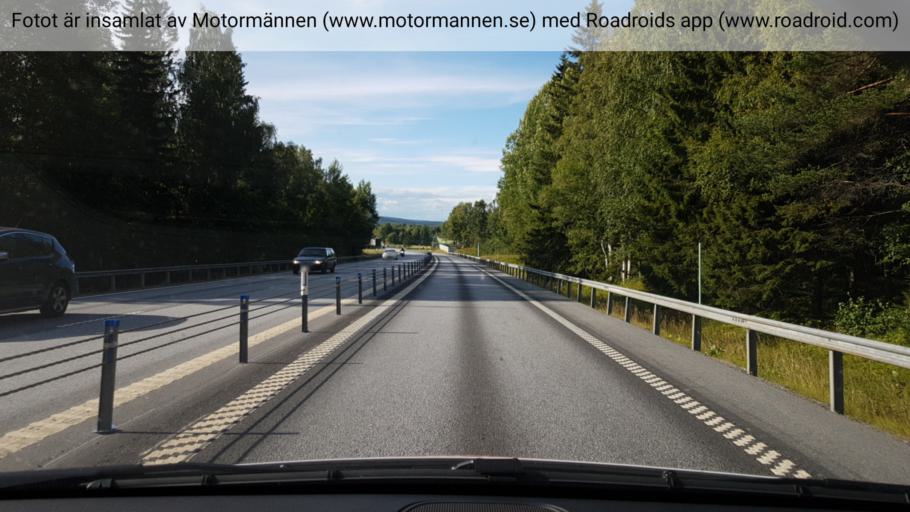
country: SE
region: Vaesterbotten
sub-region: Vannas Kommun
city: Vannasby
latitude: 63.9109
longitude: 19.8871
